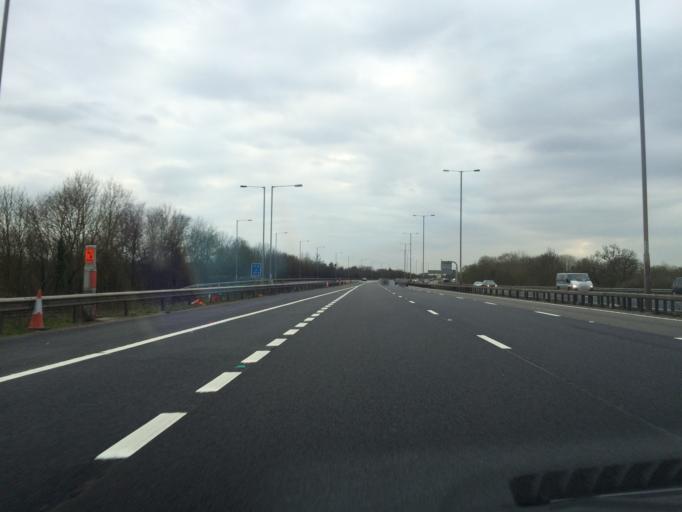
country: GB
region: England
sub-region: Wokingham
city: Winnersh
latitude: 51.4303
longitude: -0.8562
